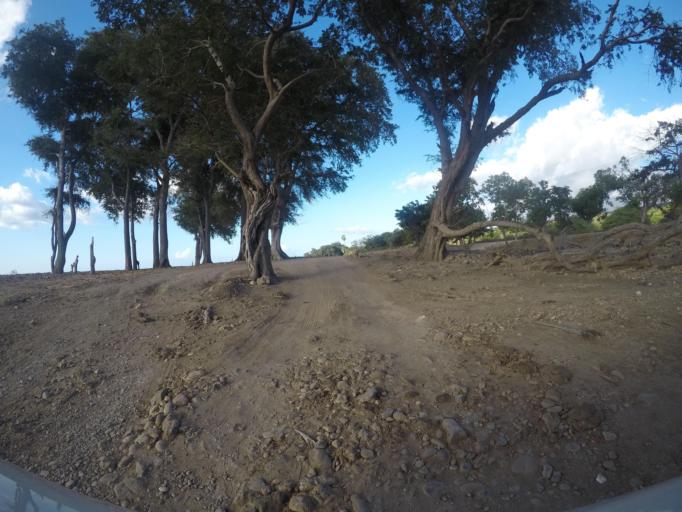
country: TL
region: Lautem
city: Lospalos
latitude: -8.3494
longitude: 126.9206
